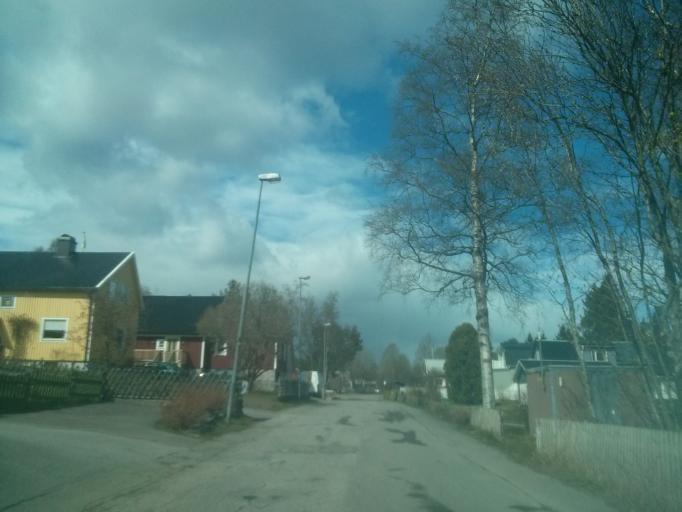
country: SE
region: Vaesternorrland
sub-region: Haernoesands Kommun
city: Haernoesand
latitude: 62.6378
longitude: 17.9136
